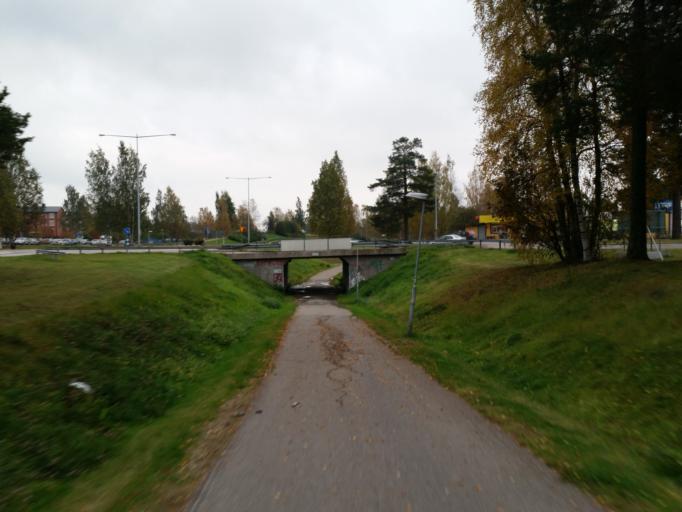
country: SE
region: Norrbotten
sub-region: Lulea Kommun
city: Lulea
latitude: 65.5783
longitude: 22.1966
